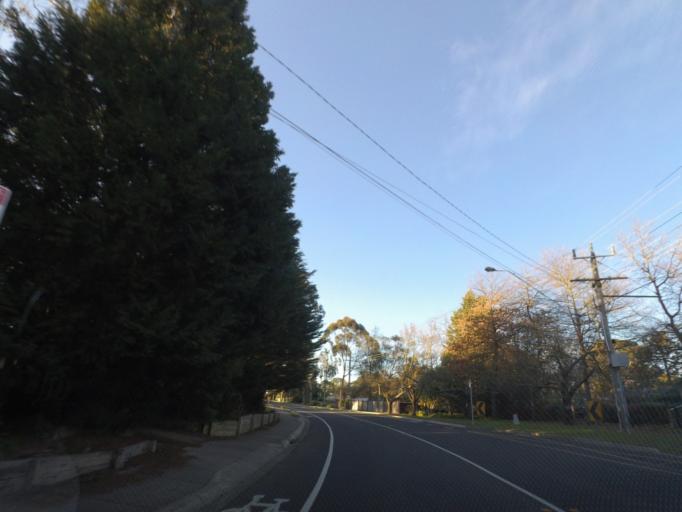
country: AU
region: Victoria
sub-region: Manningham
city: Park Orchards
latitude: -37.7813
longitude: 145.2104
